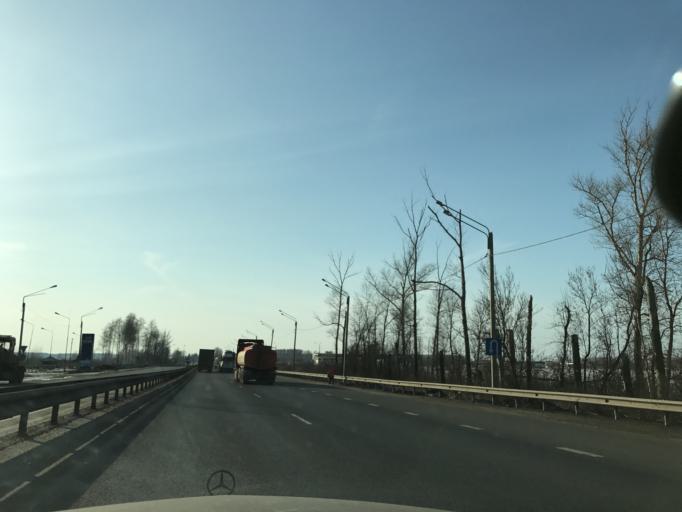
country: RU
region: Vladimir
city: Vyazniki
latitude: 56.2396
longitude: 42.0879
